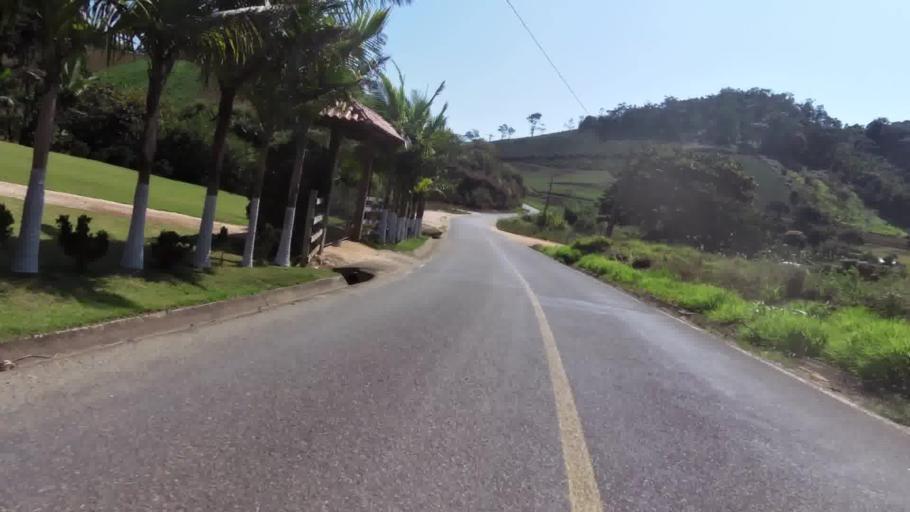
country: BR
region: Espirito Santo
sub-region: Marechal Floriano
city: Marechal Floriano
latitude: -20.4275
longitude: -40.8741
